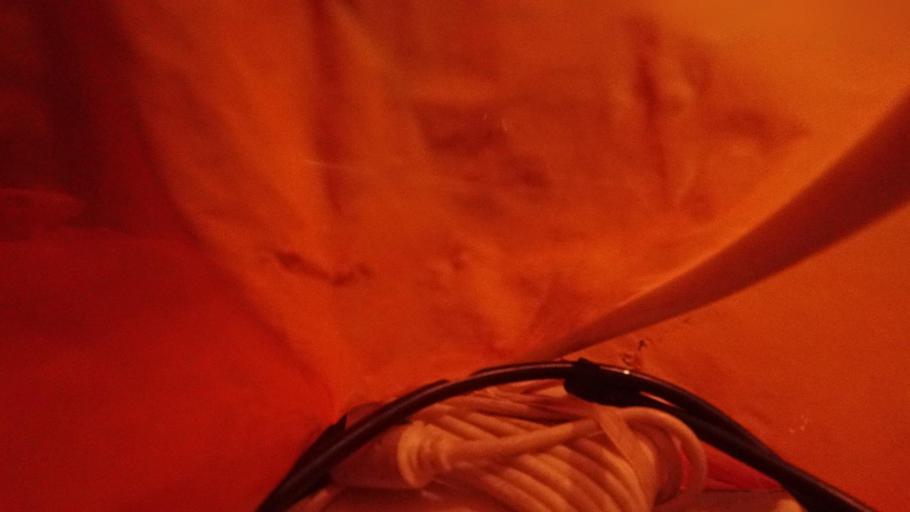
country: RU
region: Jewish Autonomous Oblast
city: Khingansk
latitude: 49.1631
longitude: 130.7699
